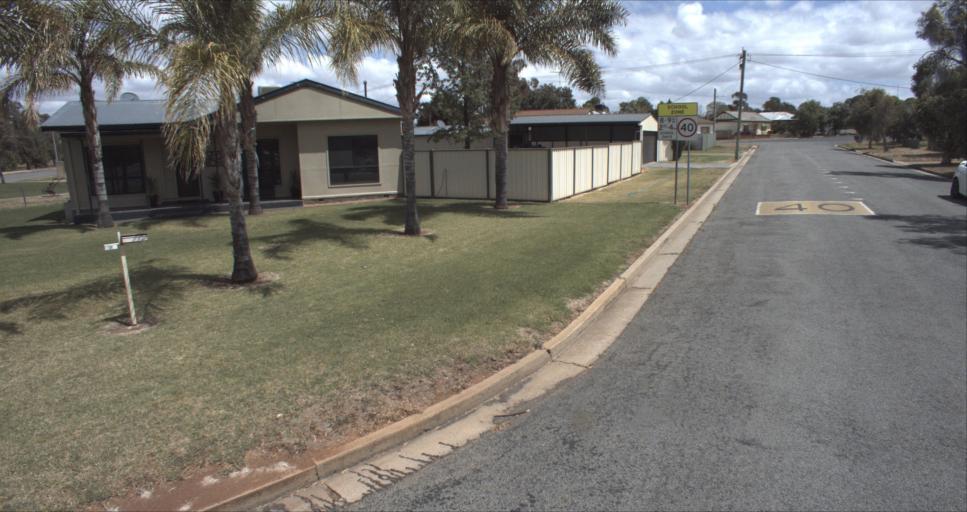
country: AU
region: New South Wales
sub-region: Leeton
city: Leeton
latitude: -34.5630
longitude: 146.3984
